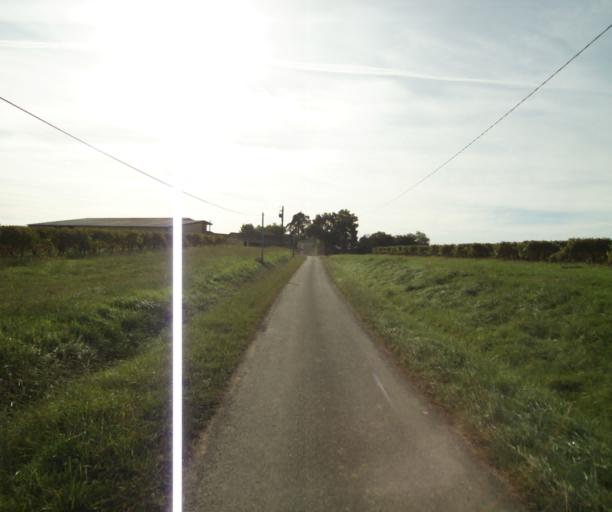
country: FR
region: Midi-Pyrenees
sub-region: Departement du Gers
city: Eauze
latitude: 43.9031
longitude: 0.1300
